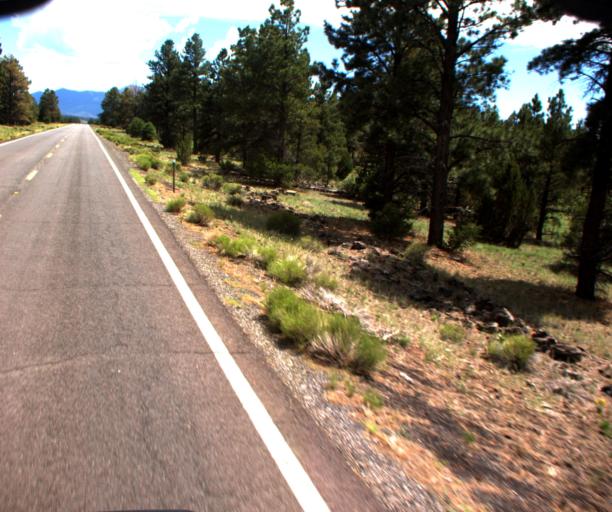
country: US
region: Arizona
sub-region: Coconino County
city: Parks
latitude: 35.4793
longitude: -111.7986
